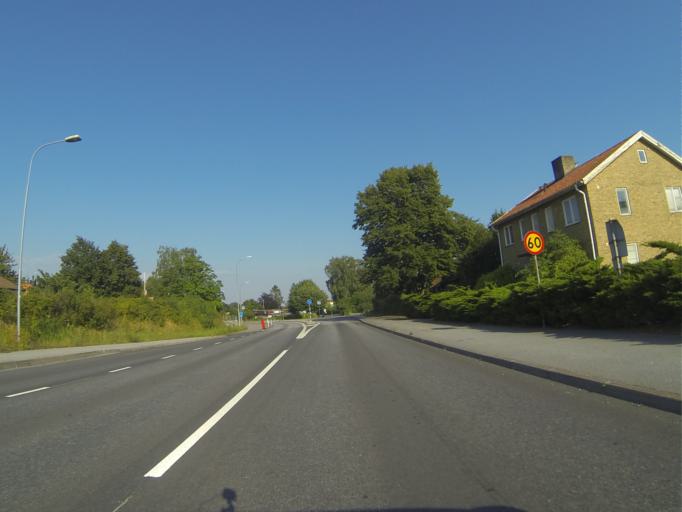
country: SE
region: Skane
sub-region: Svedala Kommun
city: Klagerup
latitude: 55.5964
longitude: 13.2522
